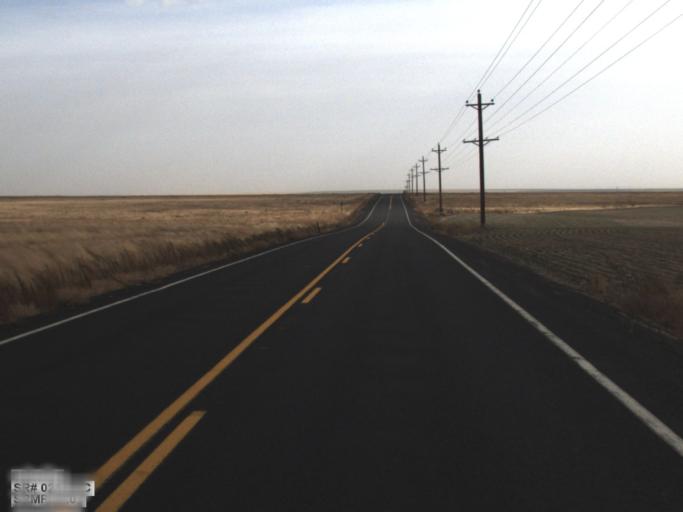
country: US
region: Washington
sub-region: Adams County
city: Ritzville
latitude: 47.4427
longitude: -118.7324
